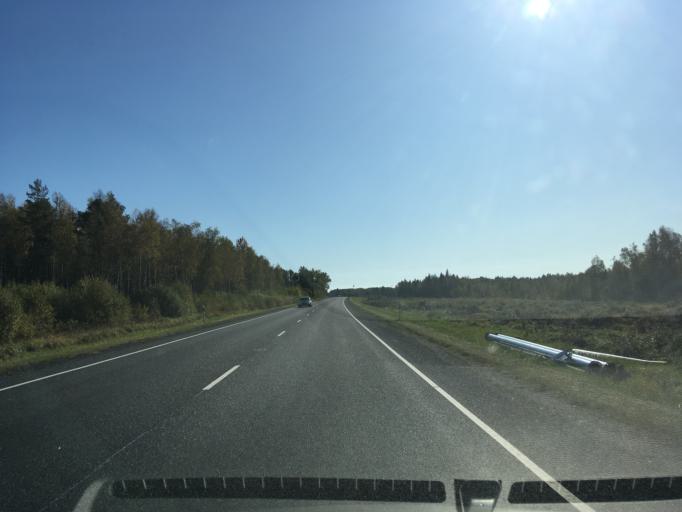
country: EE
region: Harju
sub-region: Nissi vald
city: Turba
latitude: 58.9492
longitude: 24.0833
